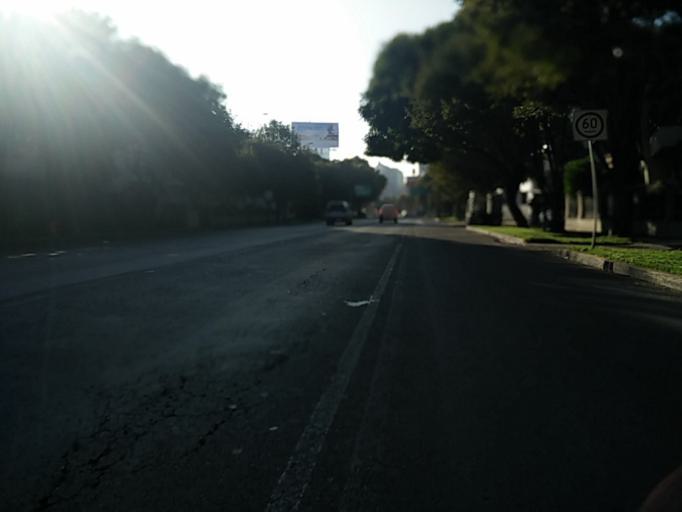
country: MX
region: Mexico City
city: Miguel Hidalgo
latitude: 19.4310
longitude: -99.1759
